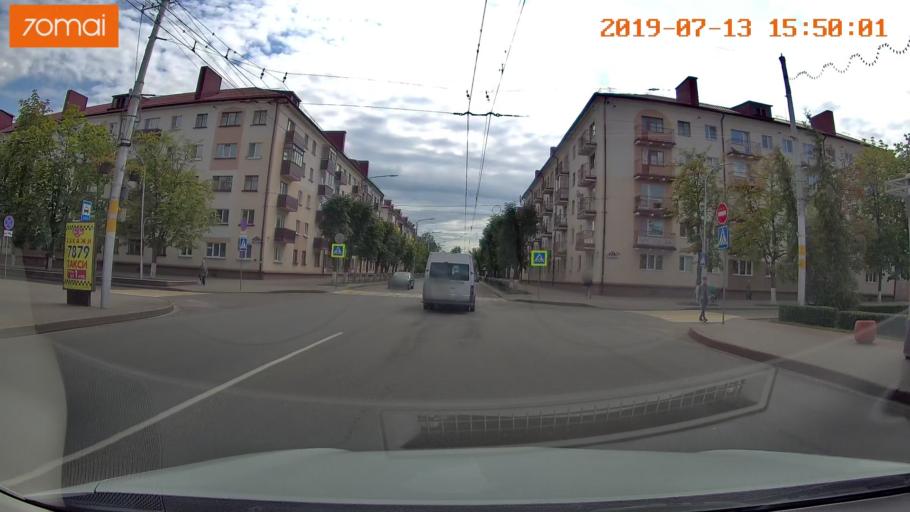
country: BY
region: Mogilev
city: Babruysk
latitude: 53.1448
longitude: 29.2269
